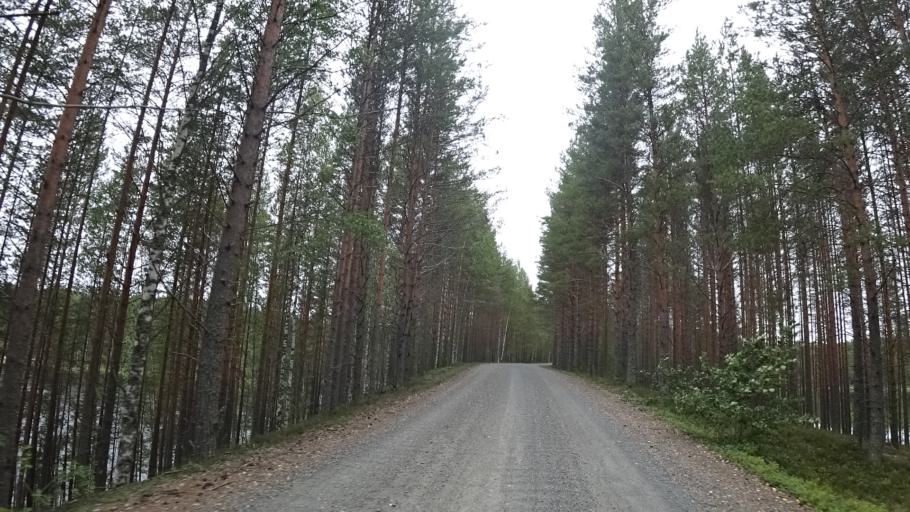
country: FI
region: North Karelia
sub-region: Joensuu
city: Ilomantsi
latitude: 62.6183
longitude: 31.1949
